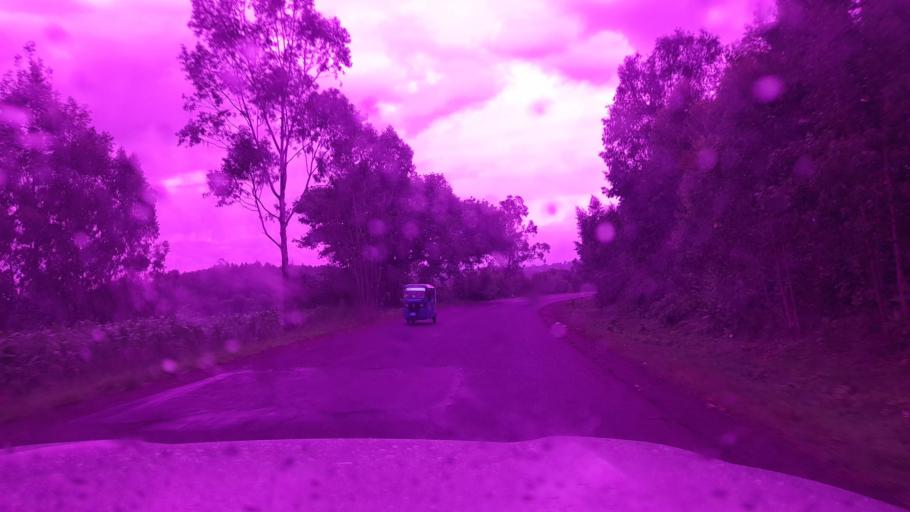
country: ET
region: Oromiya
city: Jima
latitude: 7.7108
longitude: 37.0437
